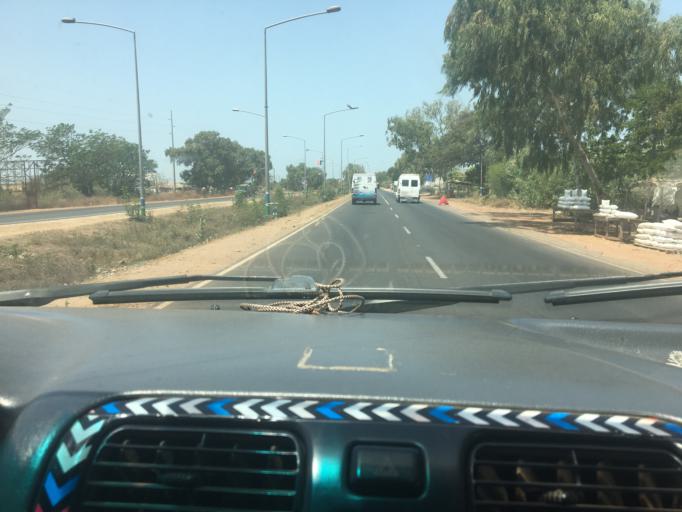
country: GM
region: Banjul
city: Bakau
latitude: 13.4683
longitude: -16.6324
